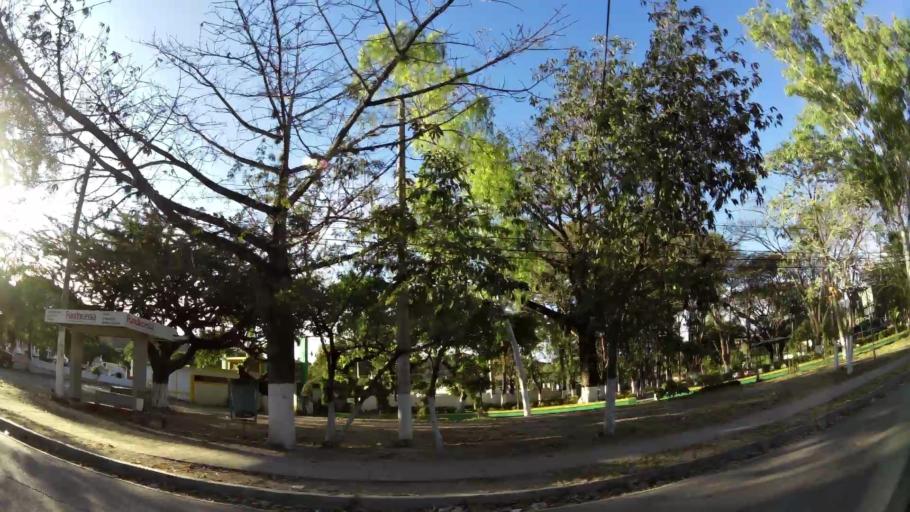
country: SV
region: Santa Ana
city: Metapan
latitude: 14.3289
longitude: -89.4532
